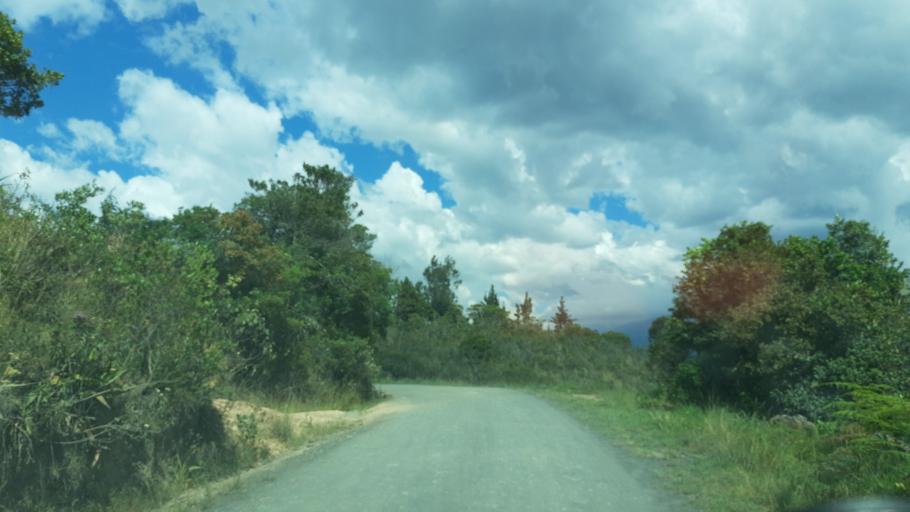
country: CO
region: Boyaca
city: La Capilla
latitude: 5.7123
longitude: -73.5356
